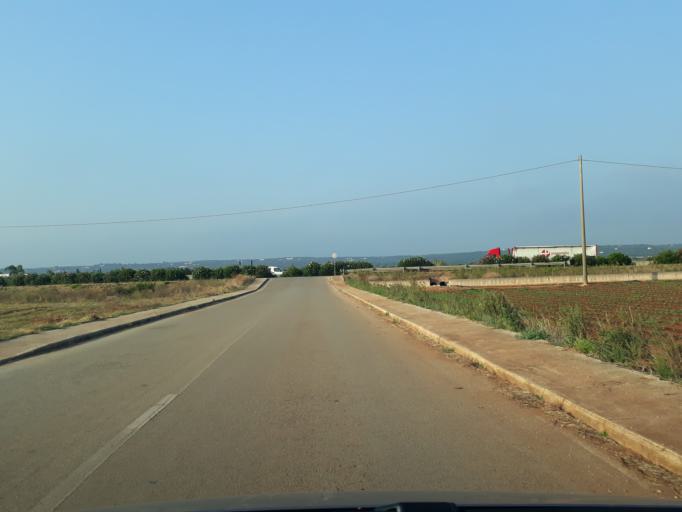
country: IT
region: Apulia
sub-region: Provincia di Brindisi
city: Carovigno
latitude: 40.7459
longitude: 17.7111
